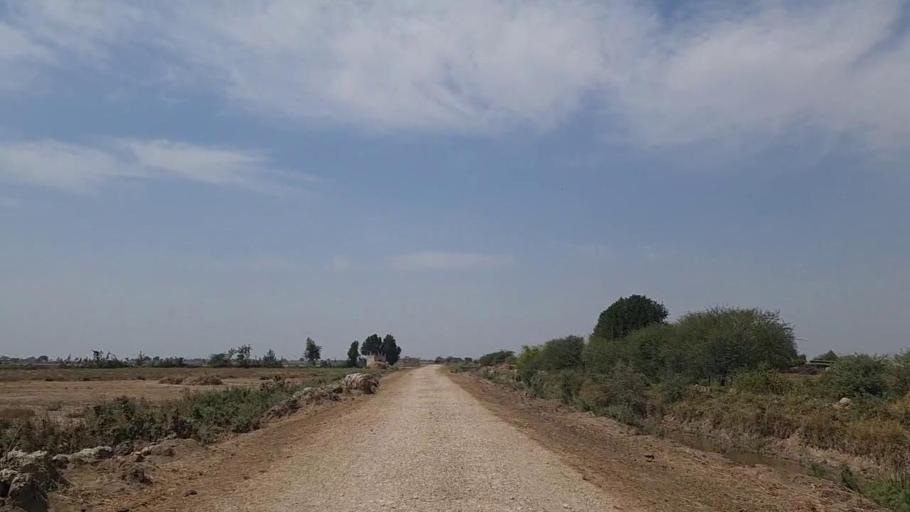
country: PK
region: Sindh
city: Jati
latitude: 24.5362
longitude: 68.3064
